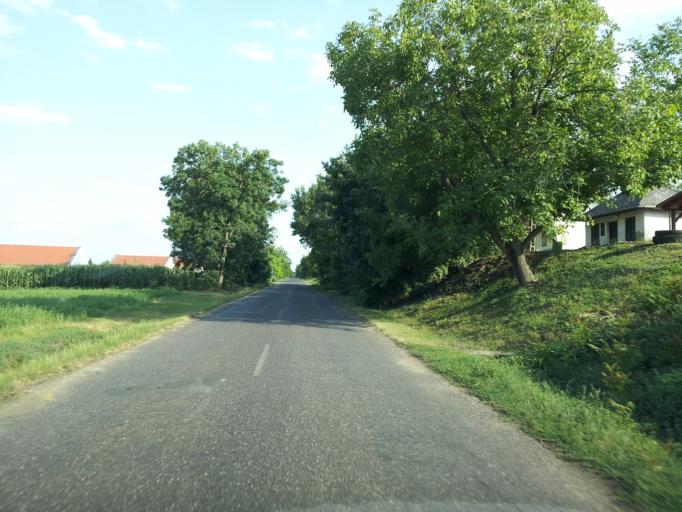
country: HU
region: Fejer
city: Lajoskomarom
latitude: 46.8350
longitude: 18.3418
